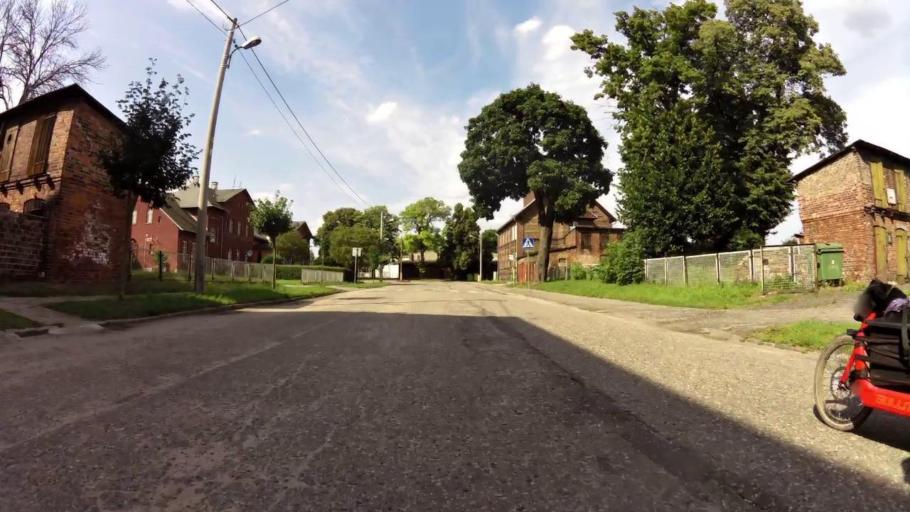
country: PL
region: West Pomeranian Voivodeship
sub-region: Powiat lobeski
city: Wegorzyno
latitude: 53.5553
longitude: 15.5300
